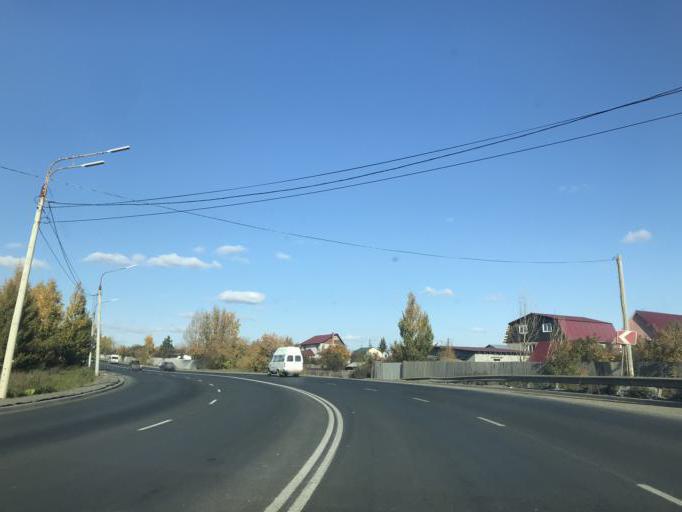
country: RU
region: Chelyabinsk
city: Roshchino
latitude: 55.2348
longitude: 61.3161
